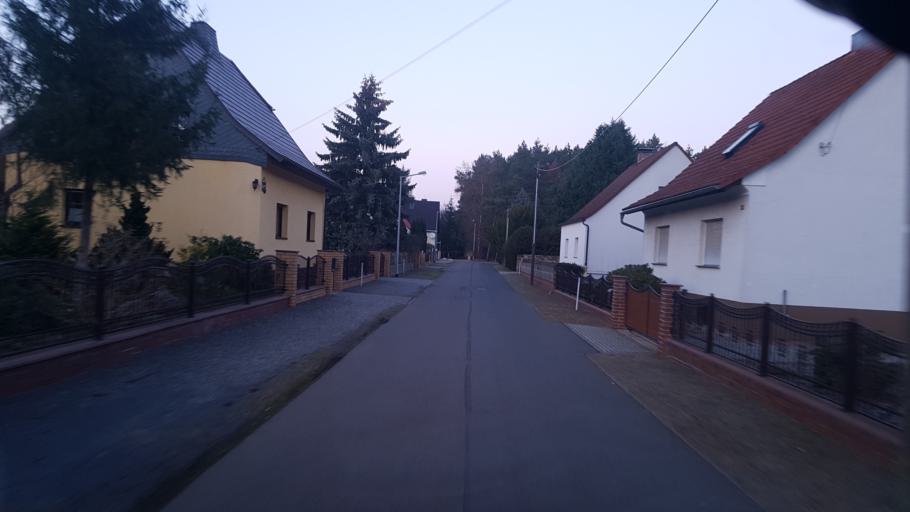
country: DE
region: Brandenburg
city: Lauchhammer
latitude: 51.5134
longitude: 13.7183
